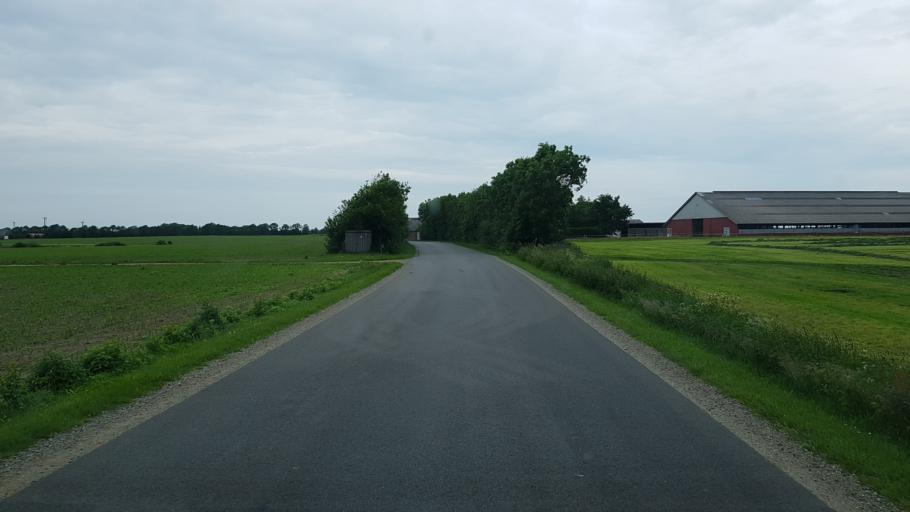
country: DK
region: South Denmark
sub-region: Varde Kommune
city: Oksbol
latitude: 55.7283
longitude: 8.3725
